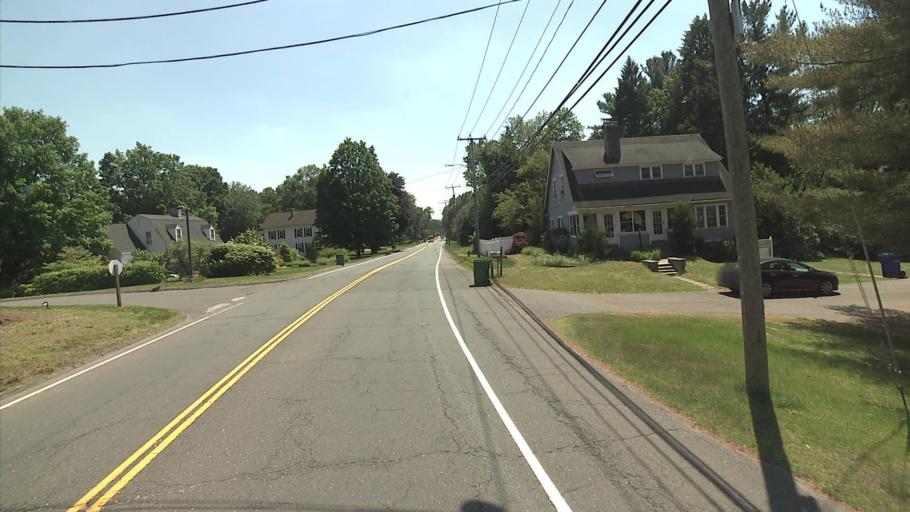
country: US
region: Connecticut
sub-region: Hartford County
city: South Windsor
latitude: 41.8199
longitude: -72.5888
